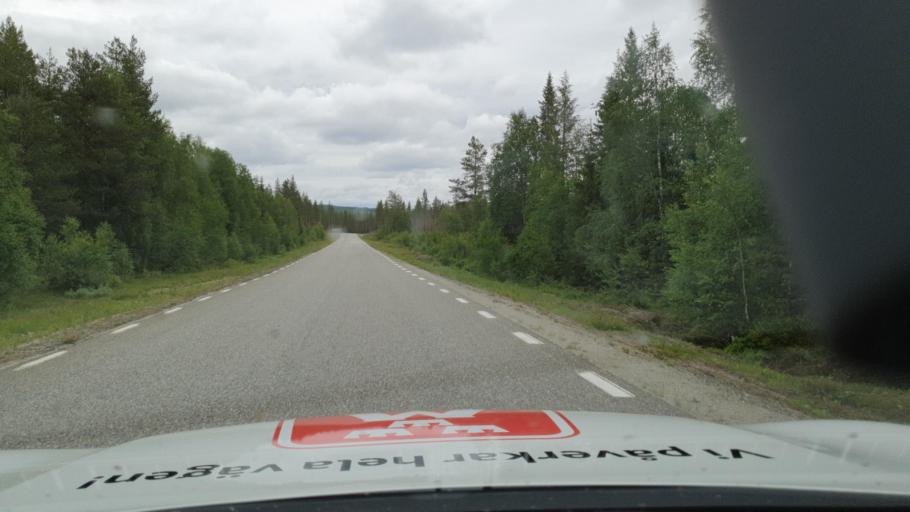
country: SE
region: Vaesterbotten
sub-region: Lycksele Kommun
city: Lycksele
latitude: 64.2080
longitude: 18.2786
